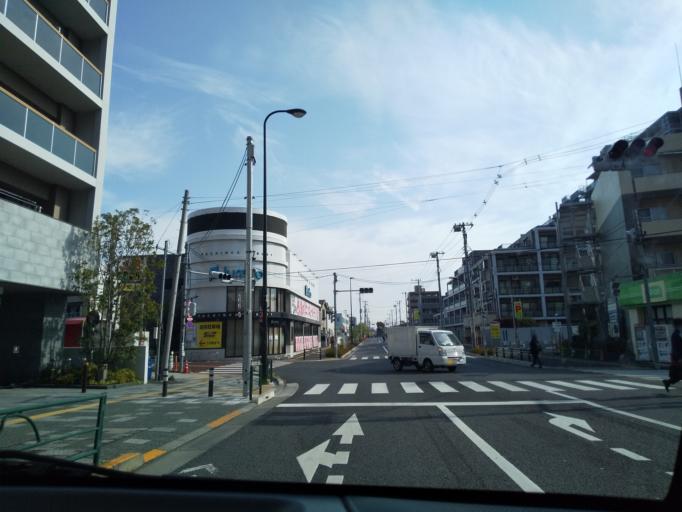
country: JP
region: Tokyo
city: Hino
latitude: 35.6802
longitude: 139.3933
